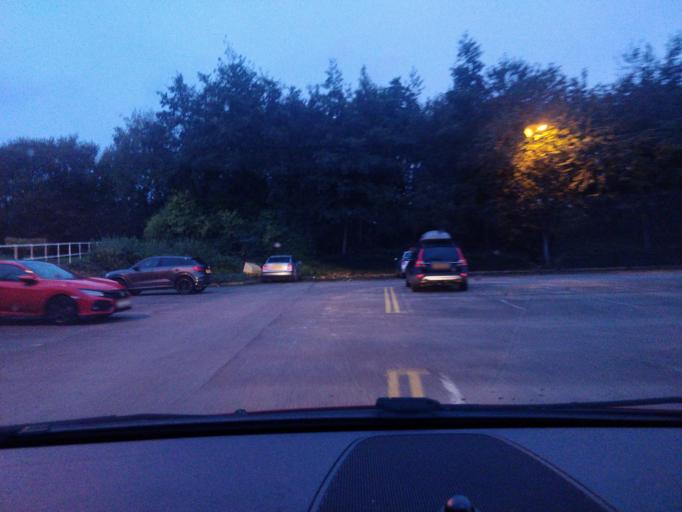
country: GB
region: England
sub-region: Lancashire
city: Ormskirk
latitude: 53.5637
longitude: -2.8688
